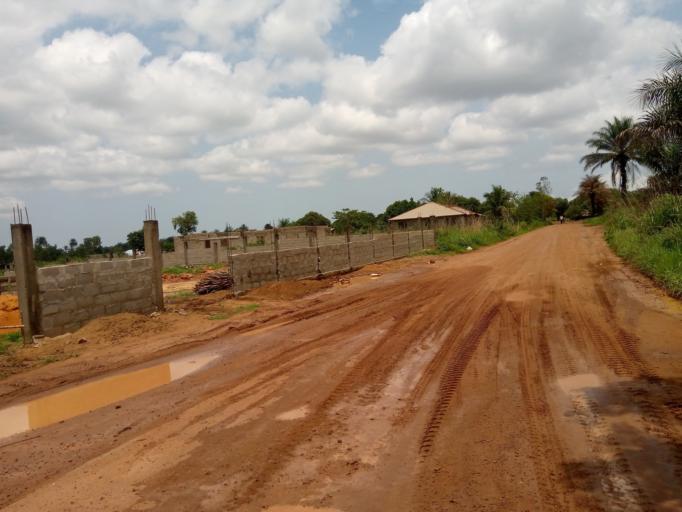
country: SL
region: Western Area
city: Waterloo
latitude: 8.3844
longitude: -12.9559
